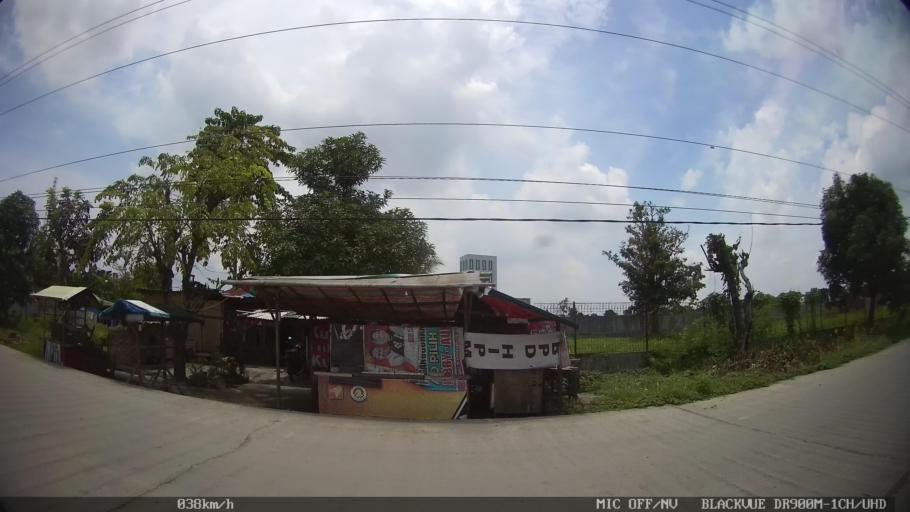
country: ID
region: North Sumatra
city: Labuhan Deli
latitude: 3.6901
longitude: 98.6841
